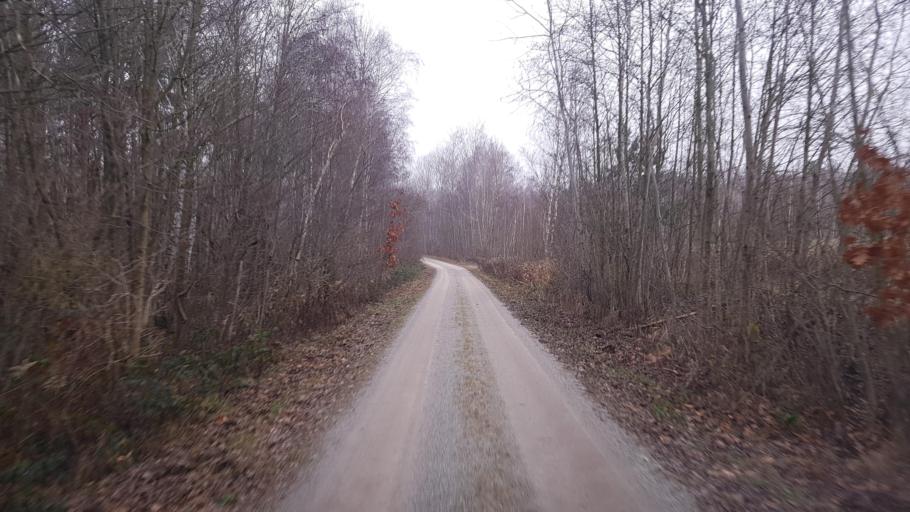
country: DE
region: Brandenburg
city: Plessa
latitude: 51.4975
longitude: 13.6484
